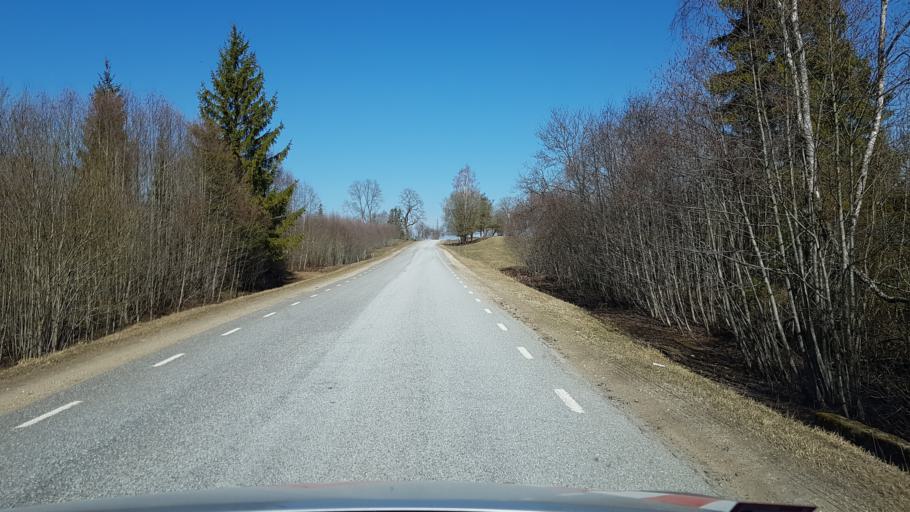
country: EE
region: Laeaene-Virumaa
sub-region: Tamsalu vald
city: Tamsalu
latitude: 59.0573
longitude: 26.1018
